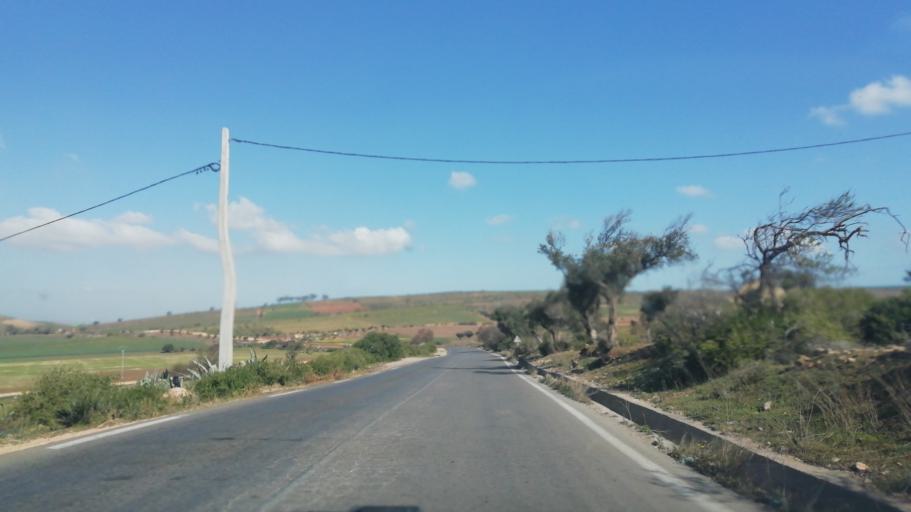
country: DZ
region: Oran
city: Ain el Bya
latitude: 35.7327
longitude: -0.2528
